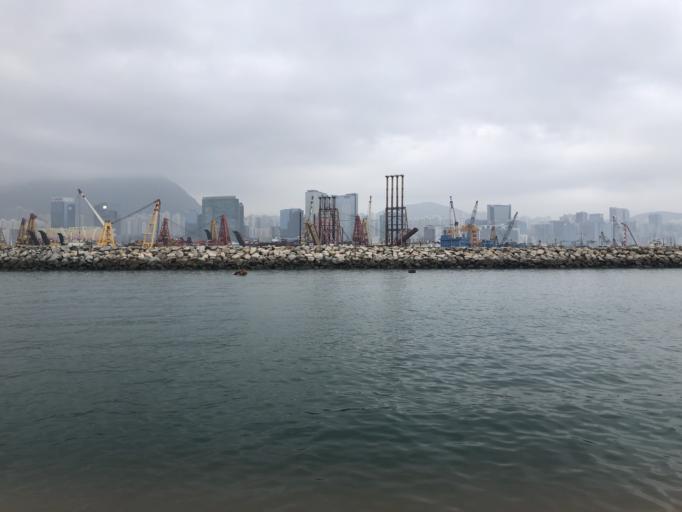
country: HK
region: Kowloon City
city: Kowloon
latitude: 22.3128
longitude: 114.1940
